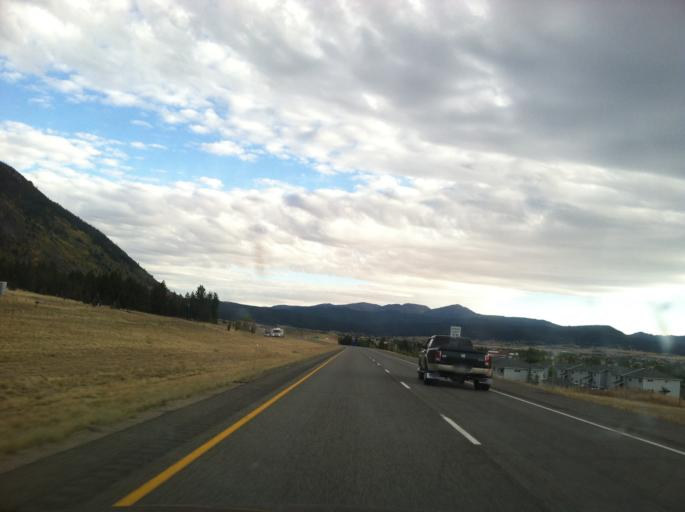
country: US
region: Montana
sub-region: Silver Bow County
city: Butte
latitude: 45.9730
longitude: -112.4762
